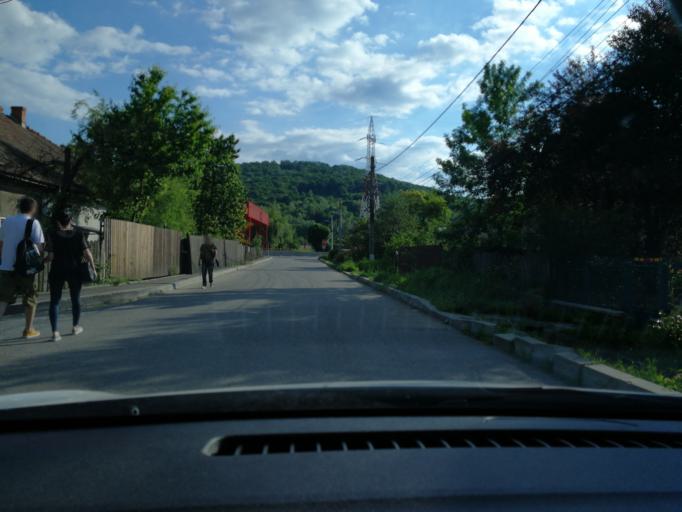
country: RO
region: Prahova
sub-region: Municipiul Campina
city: Campina
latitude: 45.1225
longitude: 25.7263
